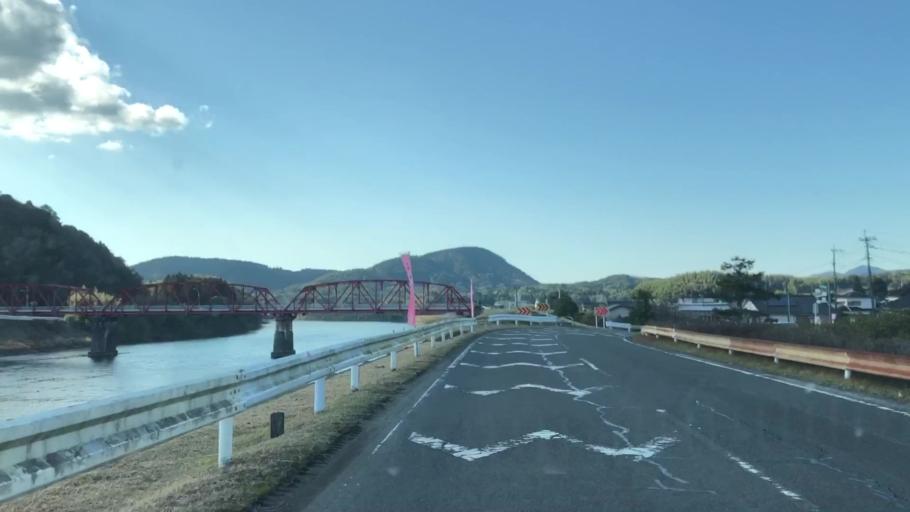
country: JP
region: Kagoshima
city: Satsumasendai
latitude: 31.8617
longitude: 130.3391
